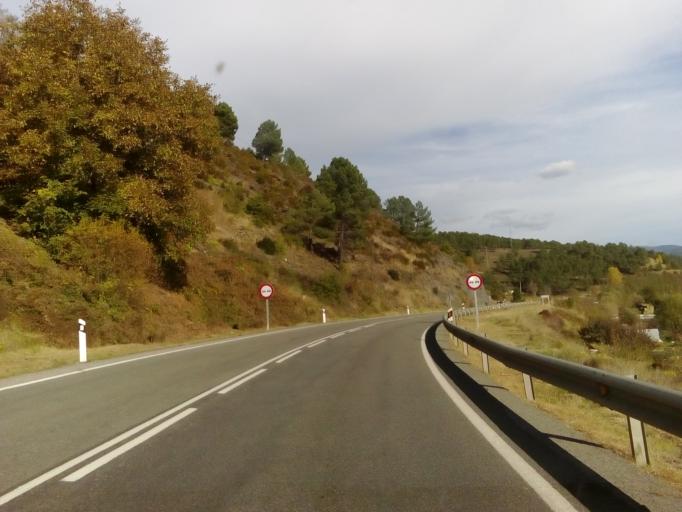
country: ES
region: Catalonia
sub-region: Provincia de Lleida
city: Bellver de Cerdanya
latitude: 42.3749
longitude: 1.7778
